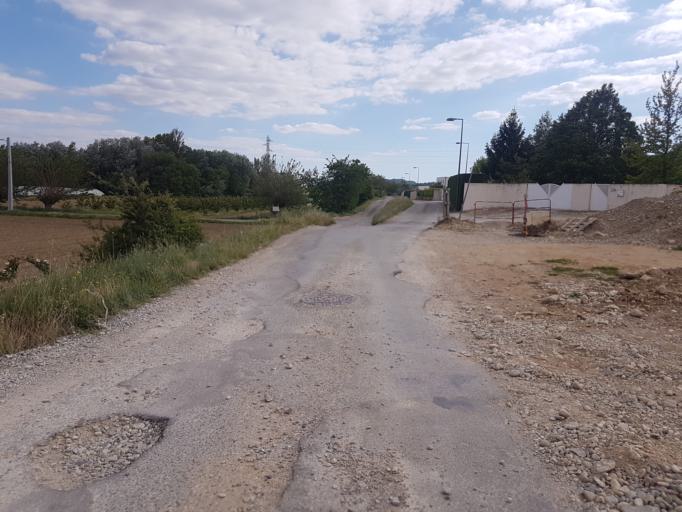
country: FR
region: Rhone-Alpes
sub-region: Departement de l'Ardeche
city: Guilherand-Granges
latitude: 44.9198
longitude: 4.8661
